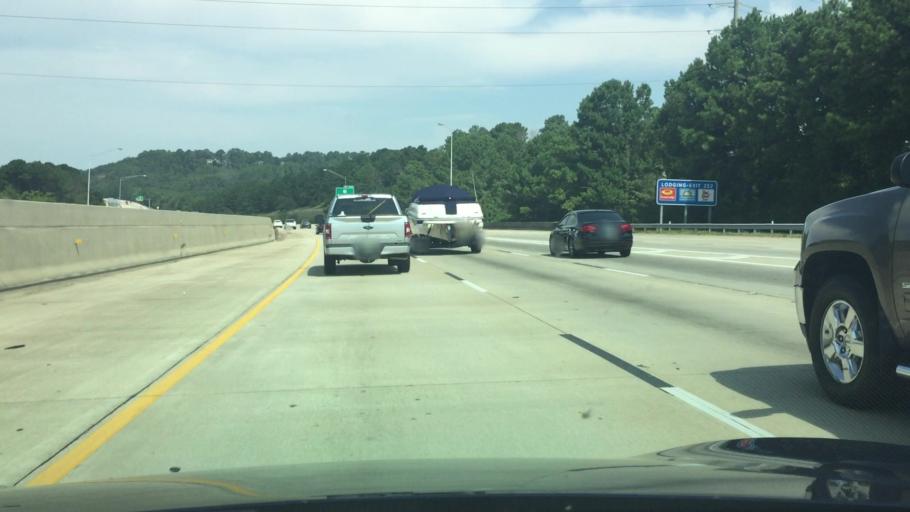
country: US
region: Alabama
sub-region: Jefferson County
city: Hoover
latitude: 33.4008
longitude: -86.7873
